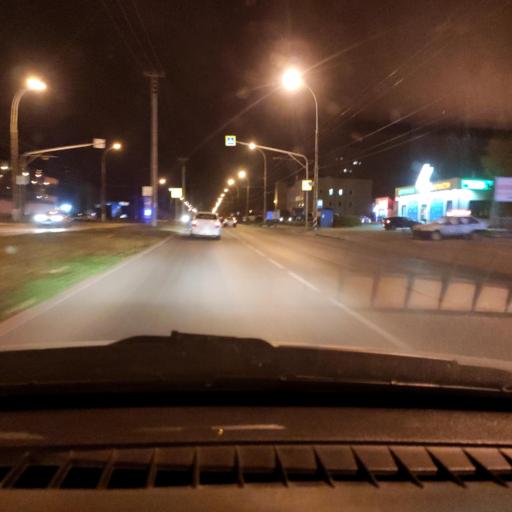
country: RU
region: Samara
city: Tol'yatti
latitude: 53.5385
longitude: 49.2997
